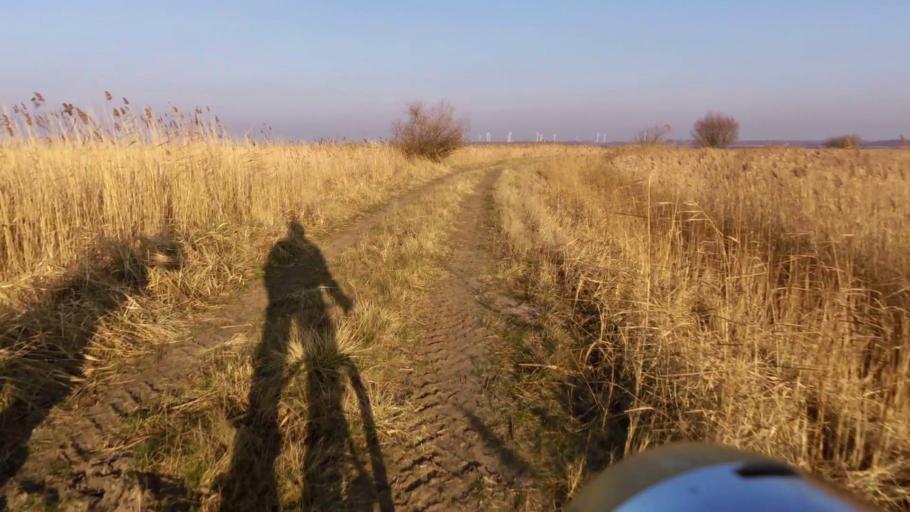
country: PL
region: West Pomeranian Voivodeship
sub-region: Powiat kamienski
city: Wolin
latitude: 53.7615
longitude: 14.5910
